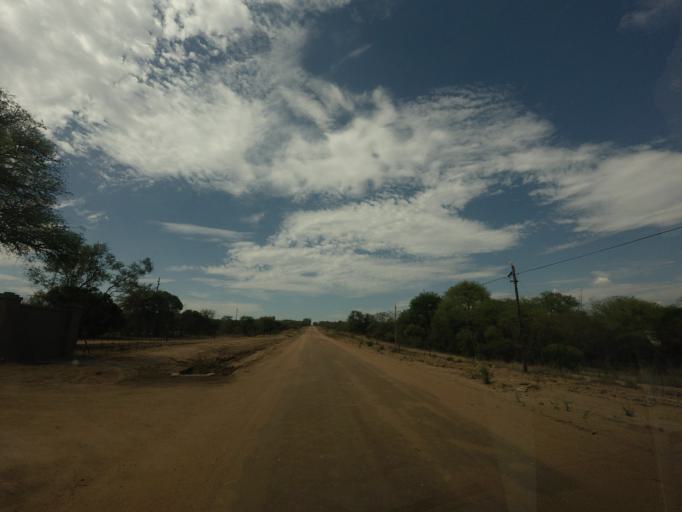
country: ZA
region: Limpopo
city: Thulamahashi
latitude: -24.5269
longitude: 31.0950
